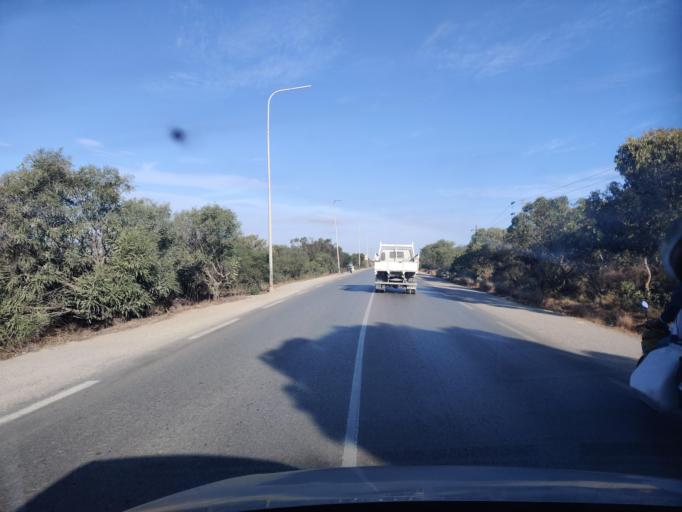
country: TN
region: Ariana
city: Ariana
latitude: 36.9409
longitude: 10.2490
